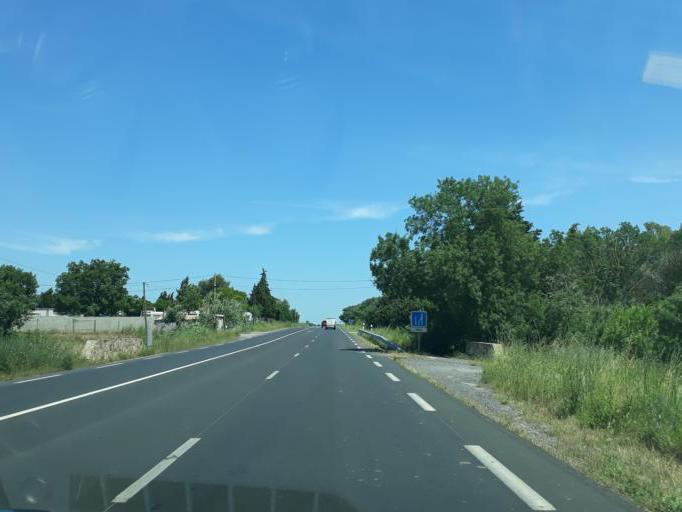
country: FR
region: Languedoc-Roussillon
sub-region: Departement de l'Herault
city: Portiragnes
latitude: 43.3139
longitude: 3.3533
